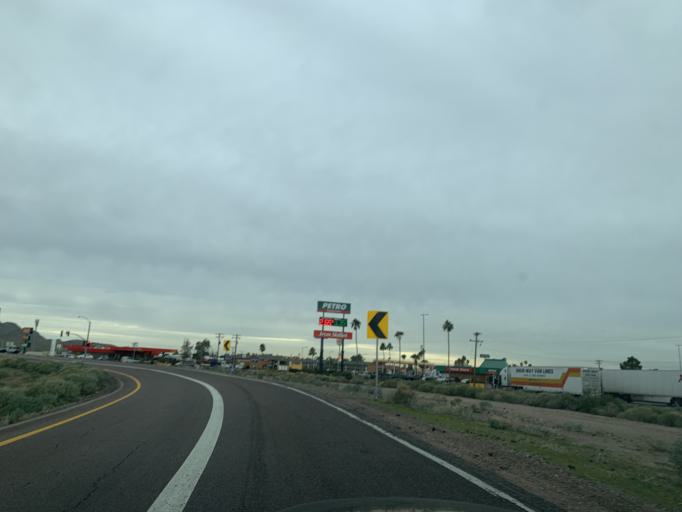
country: US
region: Arizona
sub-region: Pinal County
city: Arizona City
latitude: 32.8108
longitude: -111.6694
